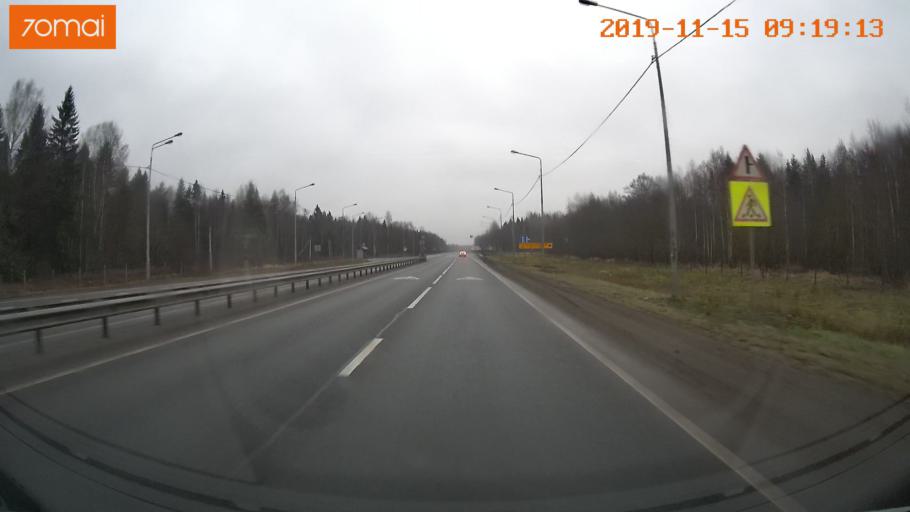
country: RU
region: Vologda
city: Tonshalovo
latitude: 59.2820
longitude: 38.0121
